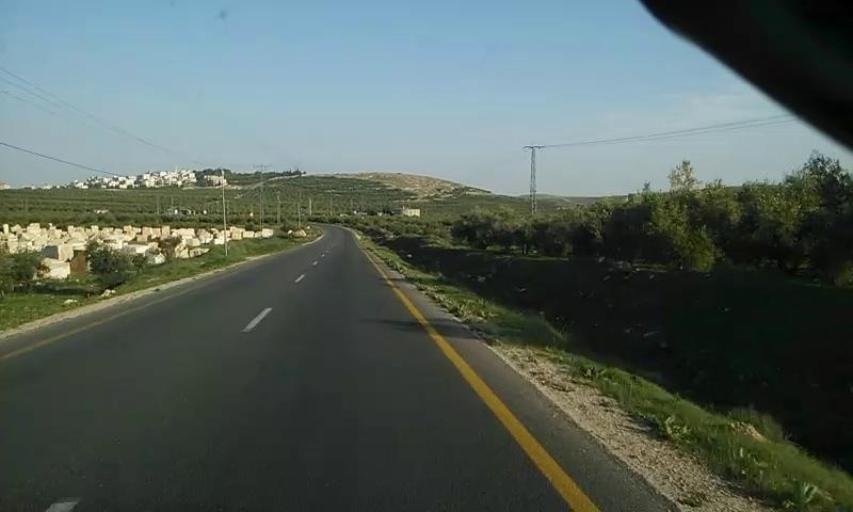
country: PS
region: West Bank
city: Marah Rabbah
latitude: 31.6411
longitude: 35.1992
